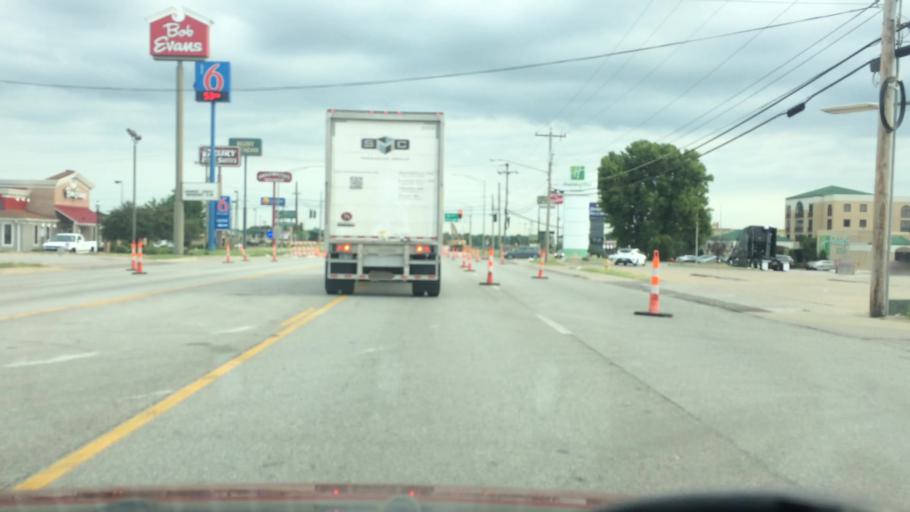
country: US
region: Missouri
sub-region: Greene County
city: Springfield
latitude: 37.2446
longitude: -93.2608
